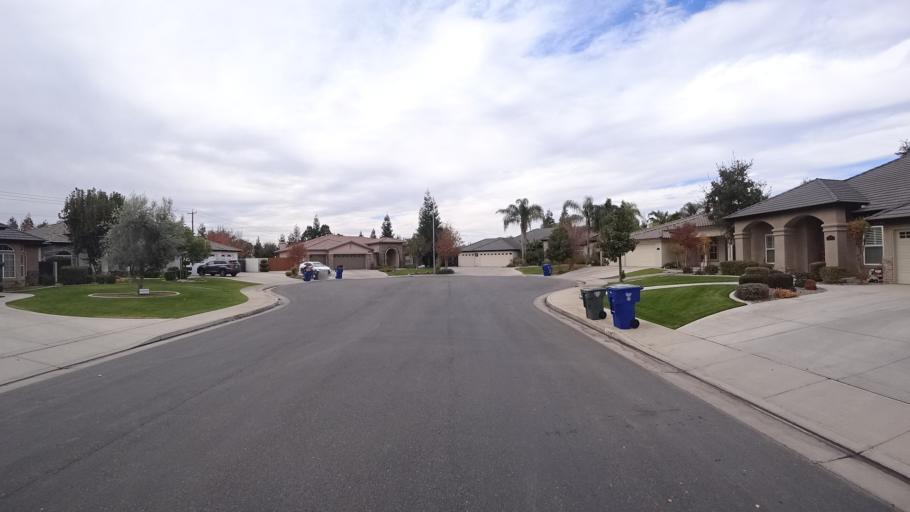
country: US
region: California
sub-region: Kern County
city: Rosedale
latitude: 35.4131
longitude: -119.1313
